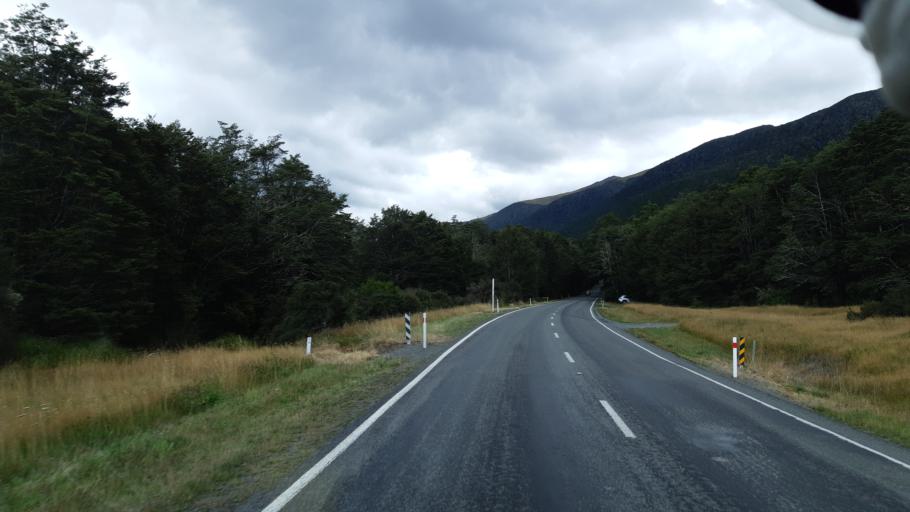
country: NZ
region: Canterbury
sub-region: Hurunui District
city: Amberley
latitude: -42.4705
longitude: 172.3970
